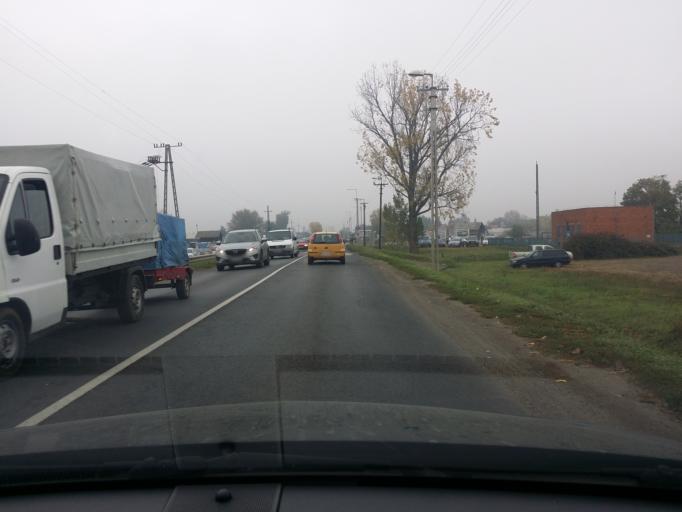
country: HU
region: Szabolcs-Szatmar-Bereg
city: Nyiregyhaza
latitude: 47.9681
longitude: 21.6961
